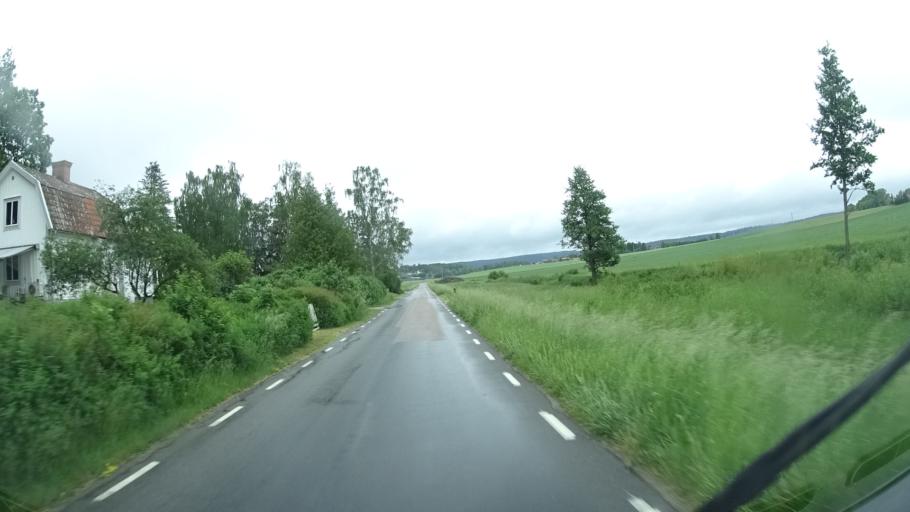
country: SE
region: Soedermanland
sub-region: Nykopings Kommun
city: Stigtomta
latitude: 58.7540
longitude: 16.7220
